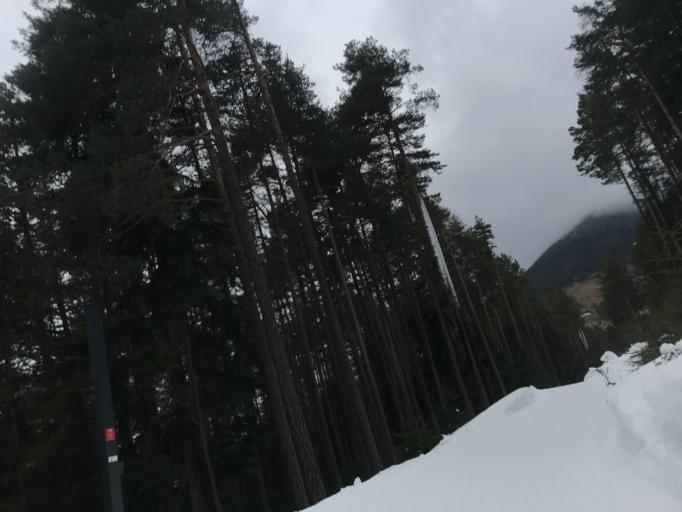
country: IT
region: Trentino-Alto Adige
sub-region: Bolzano
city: Bressanone
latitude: 46.6884
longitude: 11.6852
